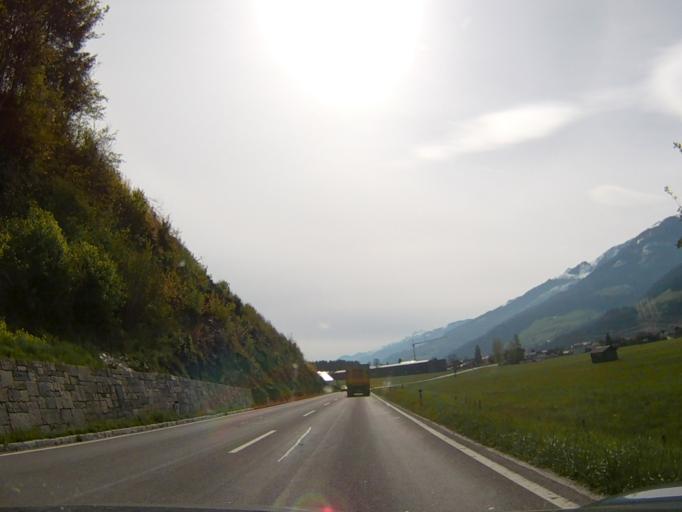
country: AT
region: Salzburg
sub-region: Politischer Bezirk Zell am See
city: Uttendorf
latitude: 47.2859
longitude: 12.6044
